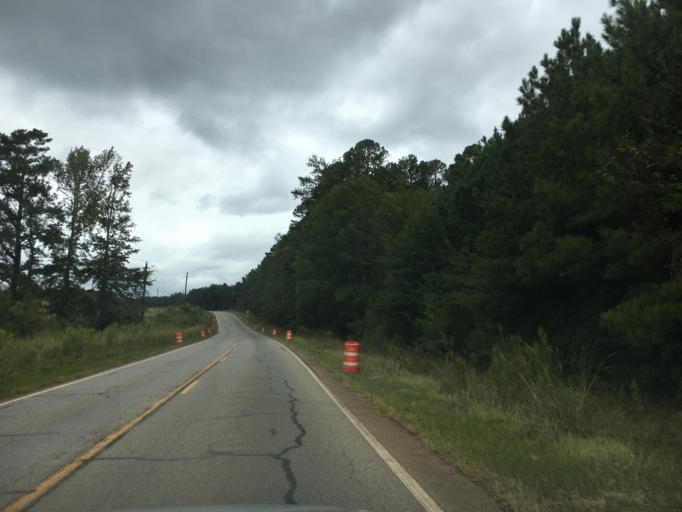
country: US
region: Georgia
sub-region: Wilkes County
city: Washington
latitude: 33.6845
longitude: -82.6404
